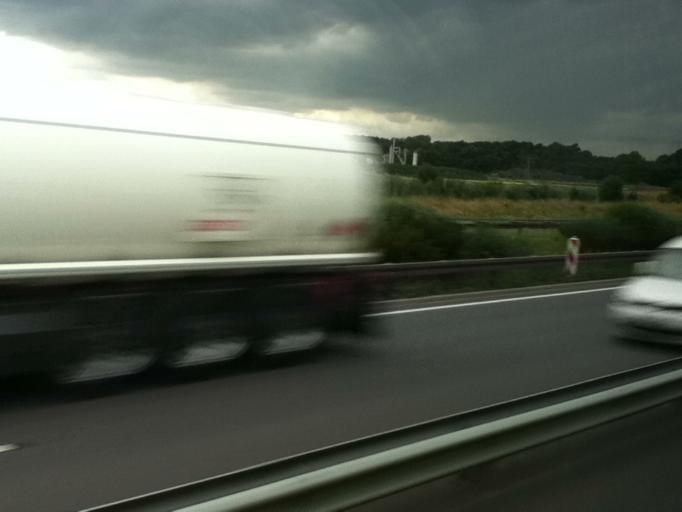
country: DE
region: Thuringia
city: Schwabhausen
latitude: 50.8952
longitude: 10.7552
